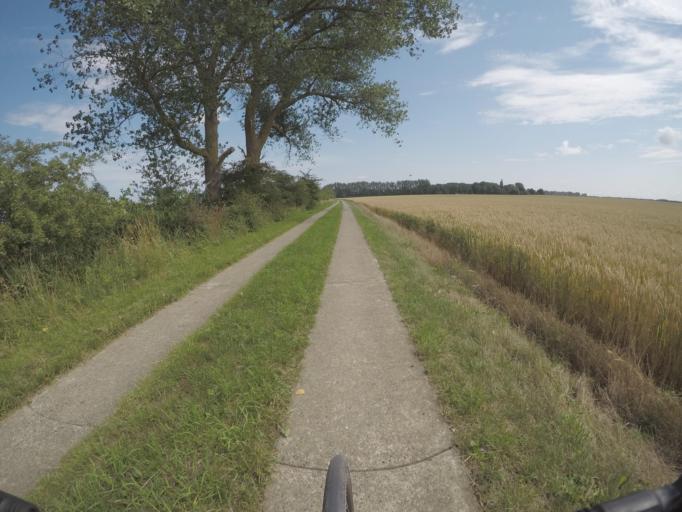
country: DE
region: Mecklenburg-Vorpommern
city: Altefahr
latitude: 54.3681
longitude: 13.1408
